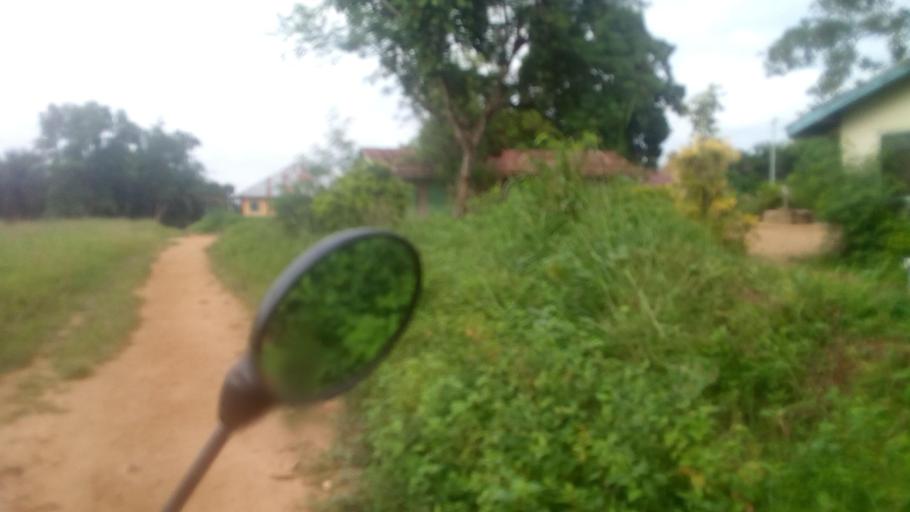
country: SL
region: Eastern Province
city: Pendembu
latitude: 8.1003
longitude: -10.6928
